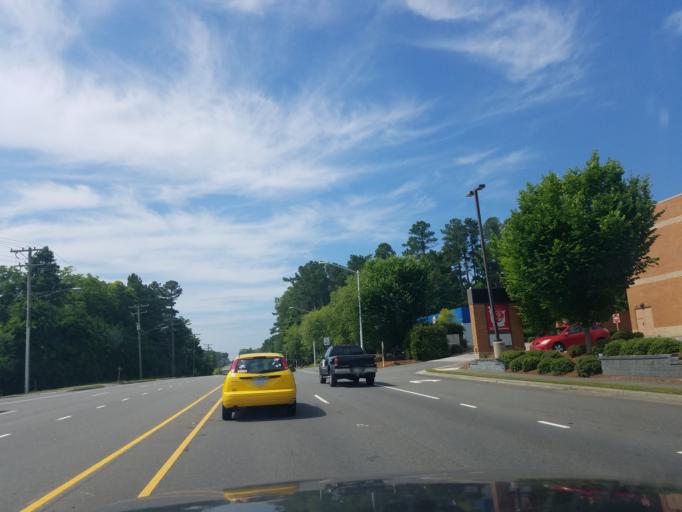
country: US
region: North Carolina
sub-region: Durham County
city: Durham
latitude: 36.0567
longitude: -78.9292
